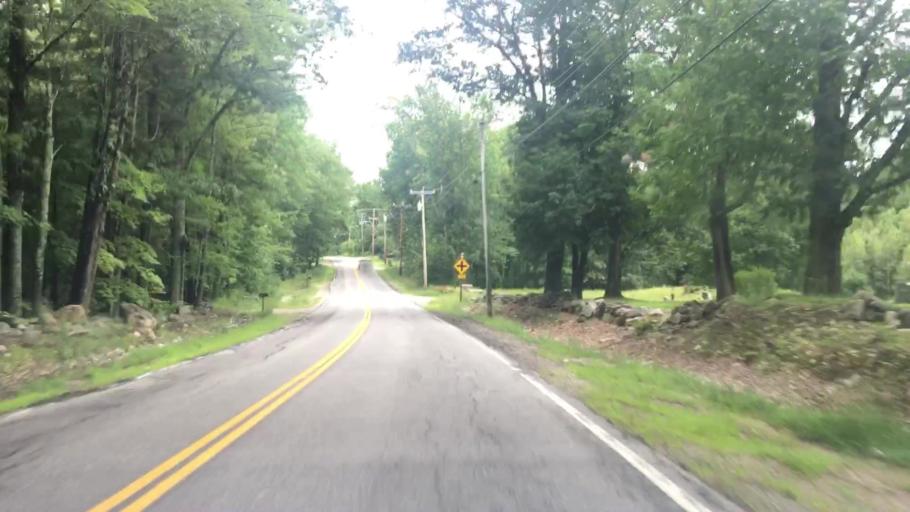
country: US
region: Maine
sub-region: York County
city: Limerick
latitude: 43.6804
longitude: -70.7884
